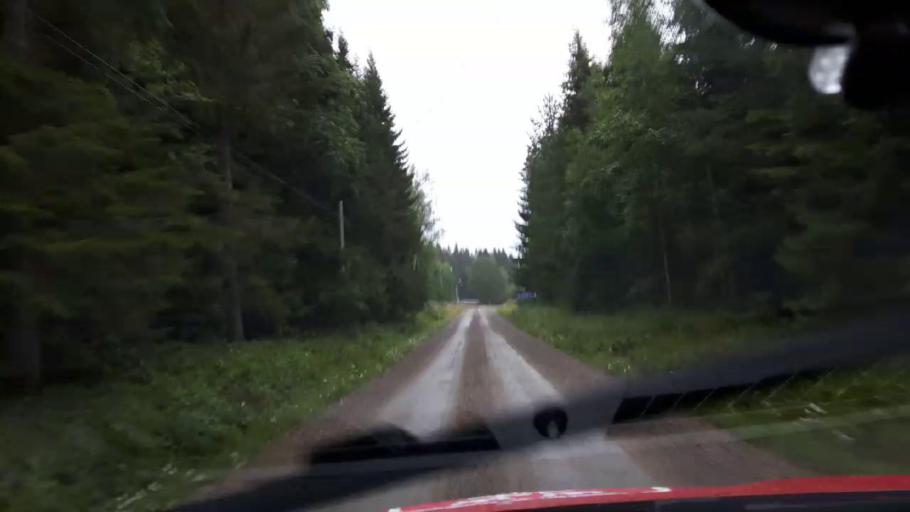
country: SE
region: Jaemtland
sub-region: OEstersunds Kommun
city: Brunflo
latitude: 62.7836
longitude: 14.9705
